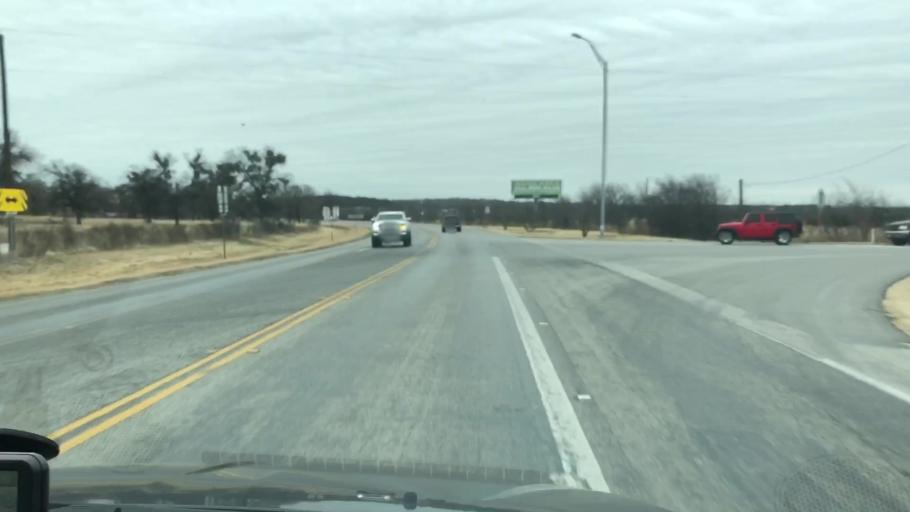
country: US
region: Texas
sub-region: Palo Pinto County
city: Mineral Wells
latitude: 32.8545
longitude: -98.0942
